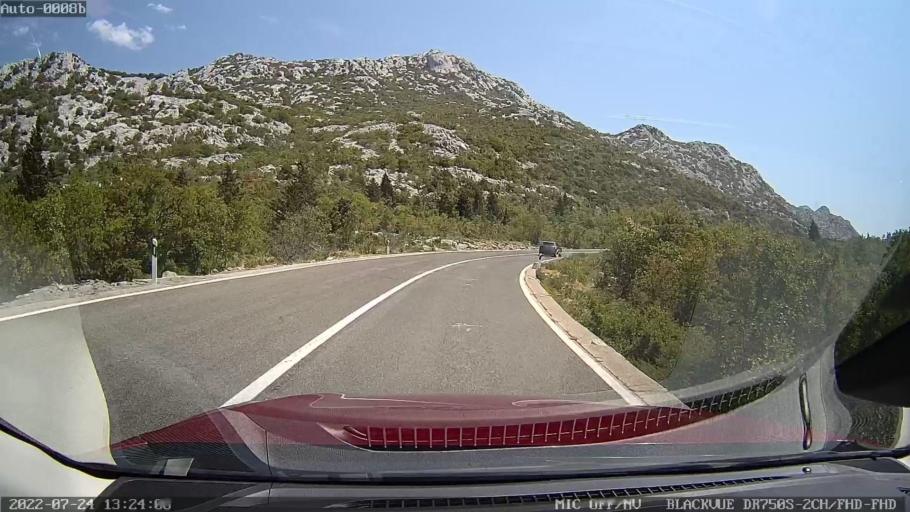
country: HR
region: Licko-Senjska
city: Novalja
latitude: 44.6624
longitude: 14.9470
